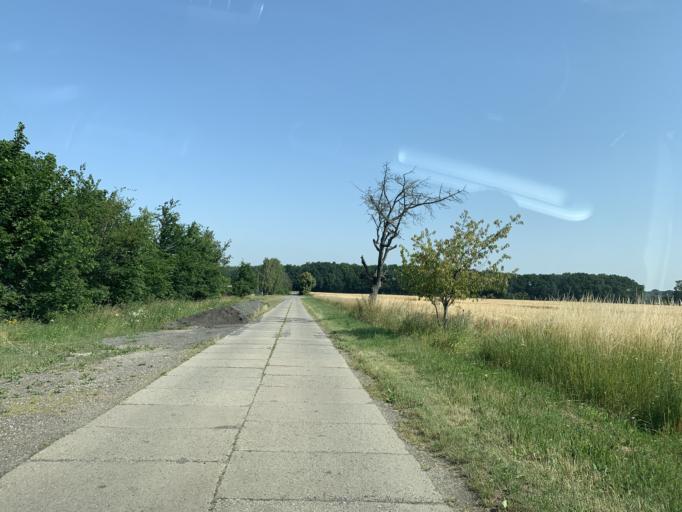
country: DE
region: Saxony-Anhalt
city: Erxleben
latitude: 52.2265
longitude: 11.2223
